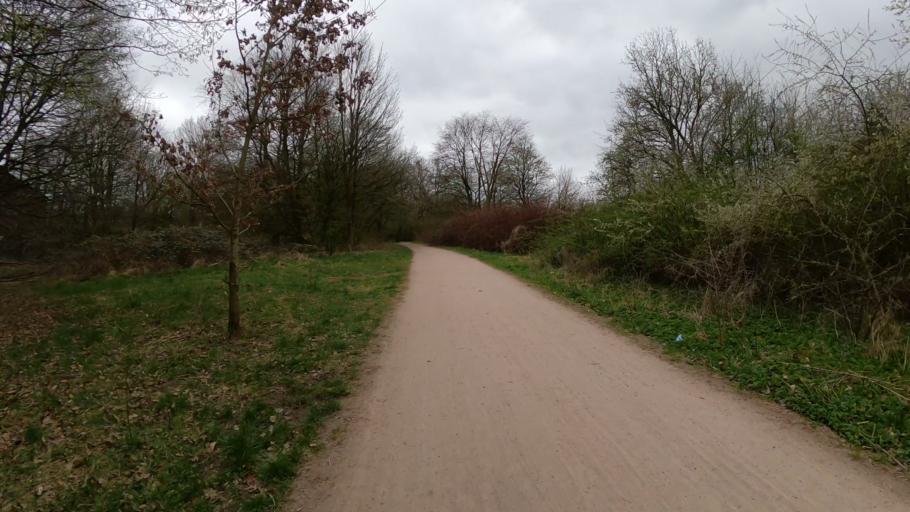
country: DE
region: Hamburg
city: Langenhorn
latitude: 53.6530
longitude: 9.9993
